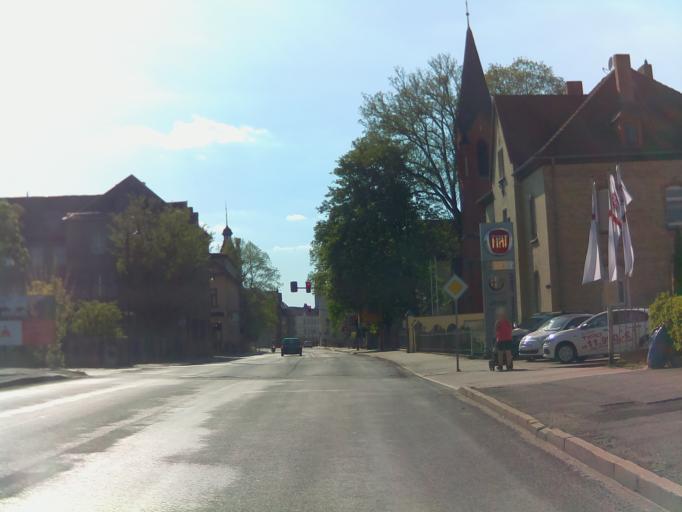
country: DE
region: Thuringia
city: Neustadt (Orla)
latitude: 50.7356
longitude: 11.7559
